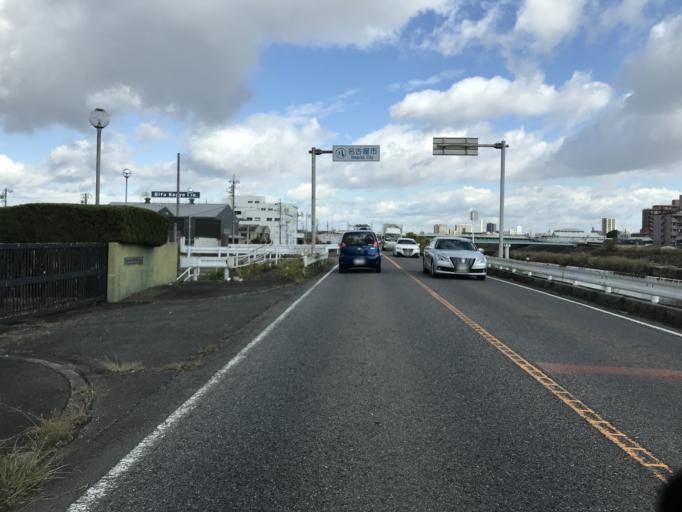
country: JP
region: Aichi
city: Nagoya-shi
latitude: 35.2134
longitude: 136.8641
